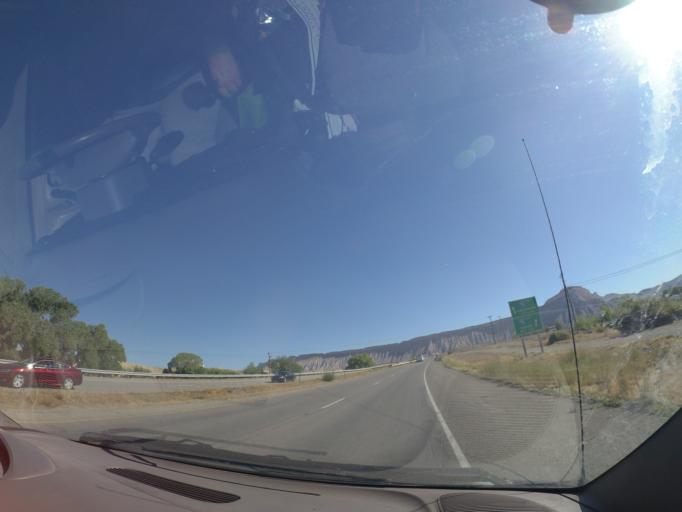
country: US
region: Colorado
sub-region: Mesa County
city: Clifton
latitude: 39.0989
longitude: -108.4486
